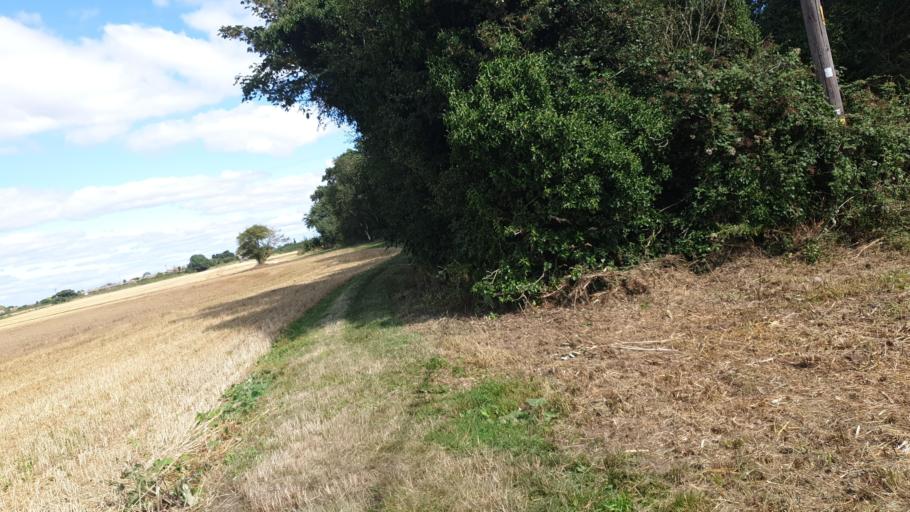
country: GB
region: England
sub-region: Essex
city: Dovercourt
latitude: 51.9112
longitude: 1.2162
